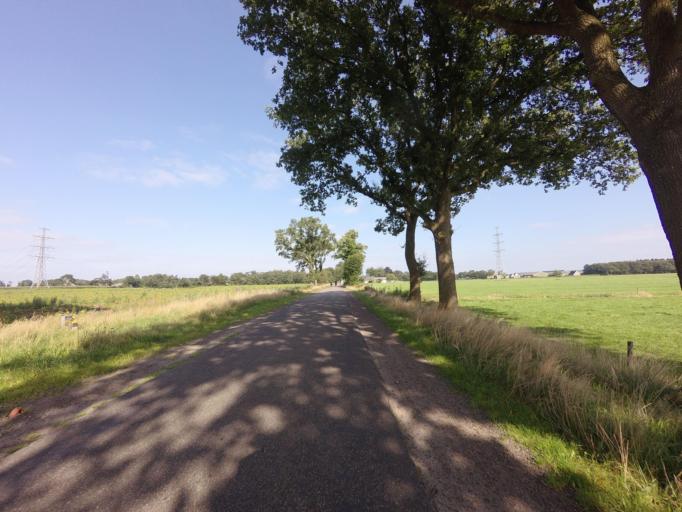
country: NL
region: Drenthe
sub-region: Gemeente Tynaarlo
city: Vries
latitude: 53.0558
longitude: 6.4918
